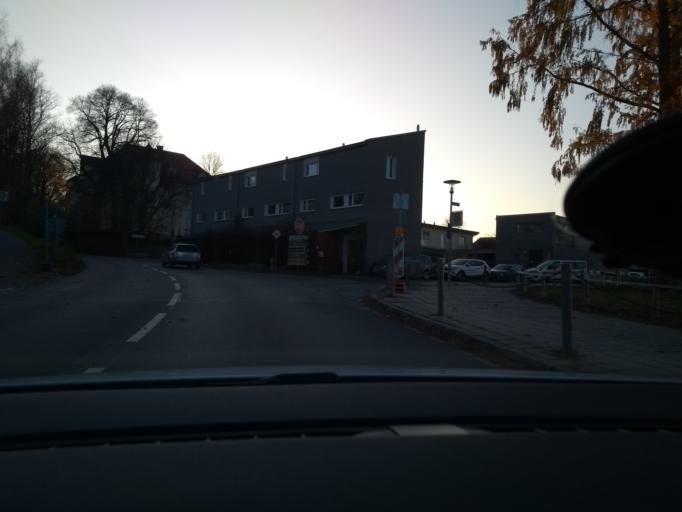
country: DE
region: Bavaria
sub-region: Upper Bavaria
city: Wasserburg am Inn
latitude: 48.0575
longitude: 12.2287
